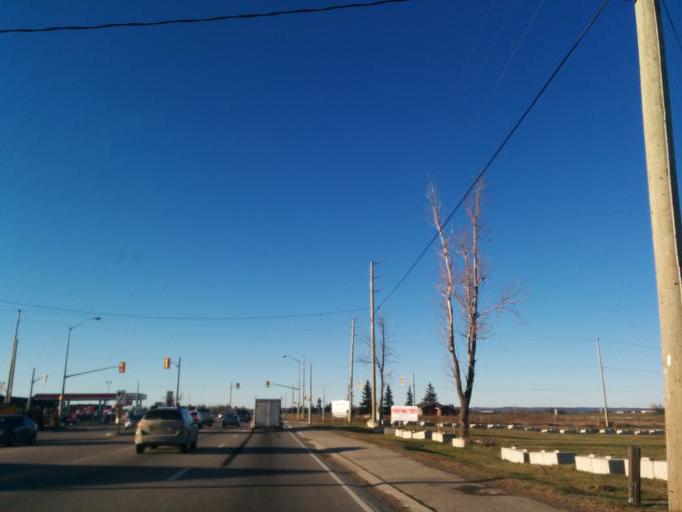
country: CA
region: Ontario
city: Brampton
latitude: 43.7729
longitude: -79.8774
